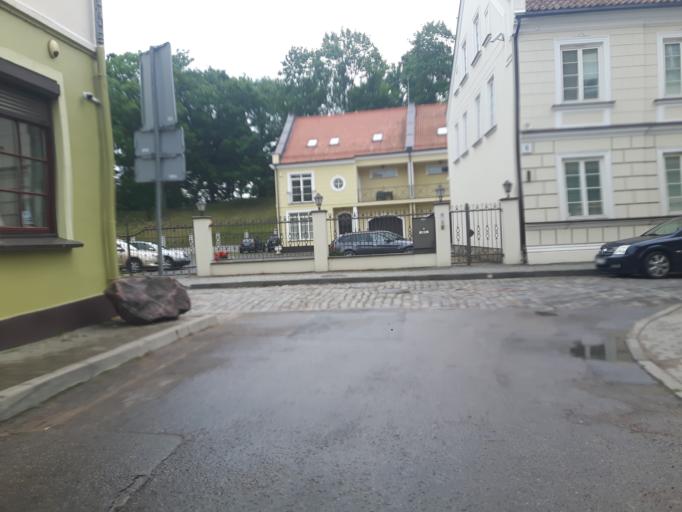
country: LT
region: Klaipedos apskritis
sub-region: Klaipeda
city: Klaipeda
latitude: 55.7083
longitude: 21.1382
